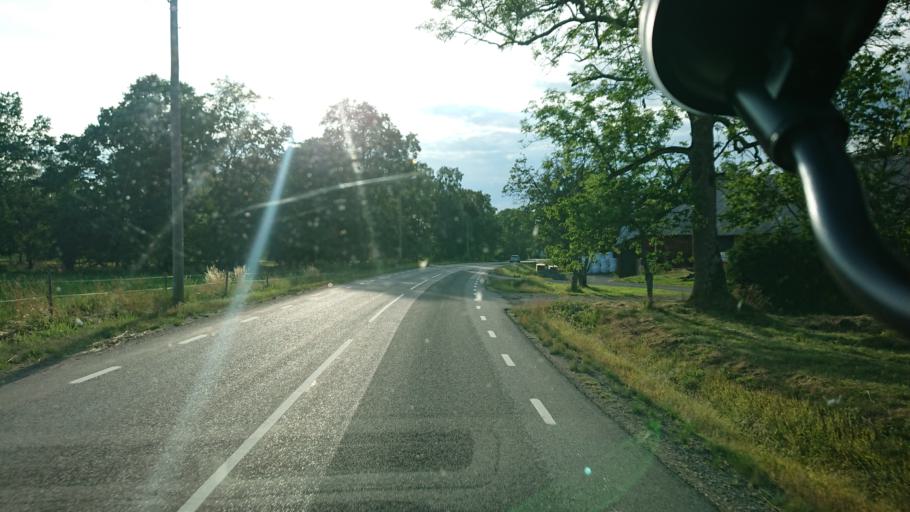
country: SE
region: Kronoberg
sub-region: Vaxjo Kommun
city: Braas
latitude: 57.0212
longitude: 15.0355
